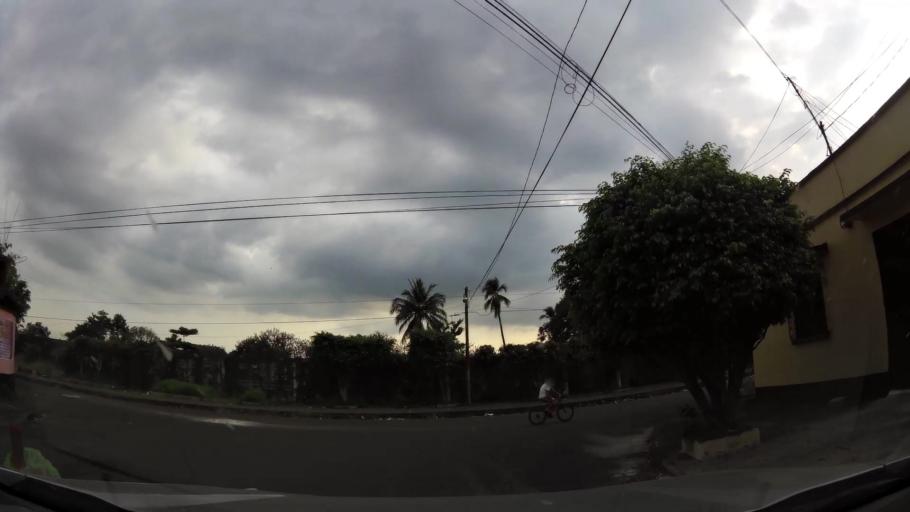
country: GT
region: Escuintla
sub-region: Municipio de Escuintla
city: Escuintla
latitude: 14.2886
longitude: -90.7827
